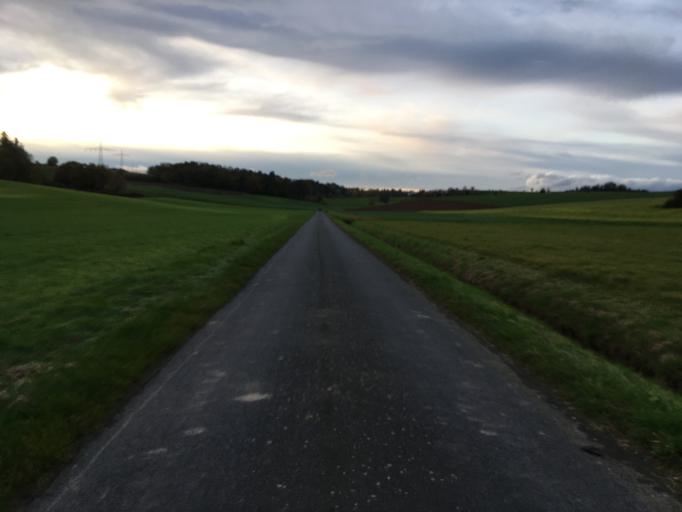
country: DE
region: Baden-Wuerttemberg
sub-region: Karlsruhe Region
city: Rosenberg
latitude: 49.3917
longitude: 9.4921
